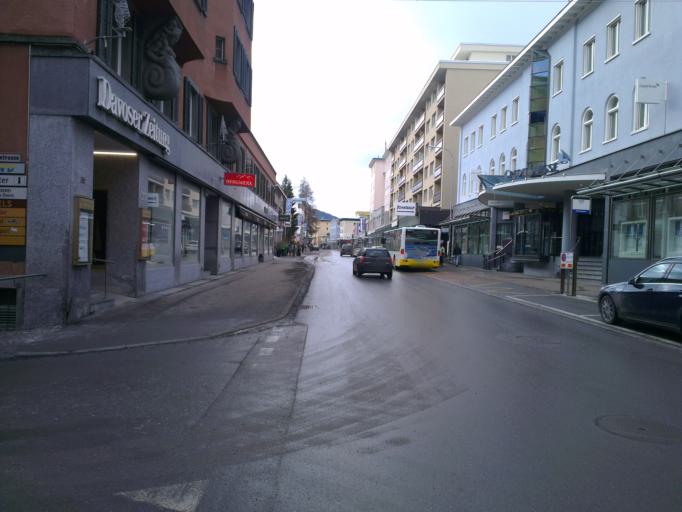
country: CH
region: Grisons
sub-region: Praettigau/Davos District
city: Davos
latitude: 46.7975
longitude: 9.8222
